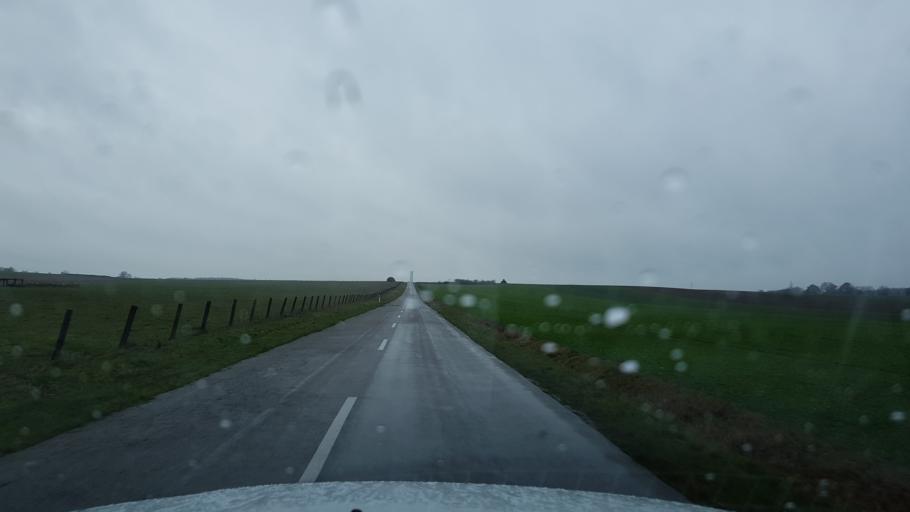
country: PL
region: West Pomeranian Voivodeship
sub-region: Powiat lobeski
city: Dobra
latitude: 53.5943
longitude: 15.3809
